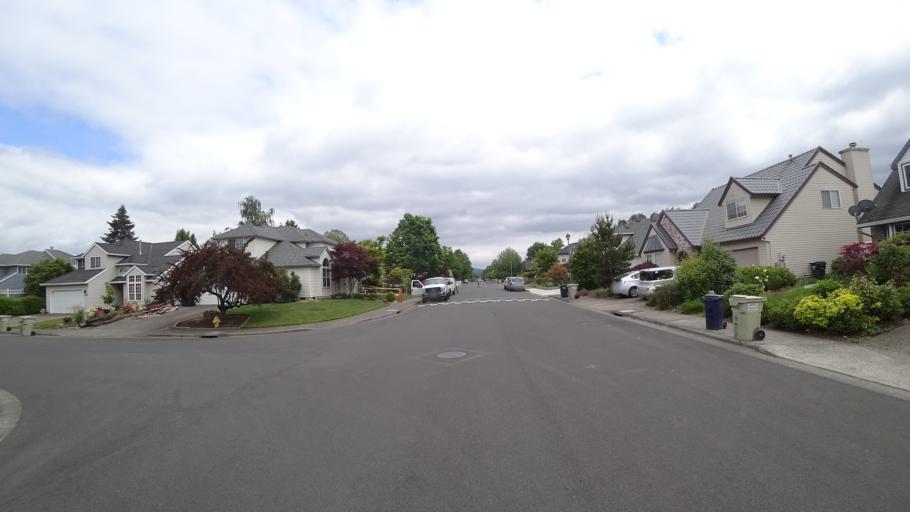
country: US
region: Oregon
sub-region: Washington County
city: Aloha
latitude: 45.5231
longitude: -122.8648
